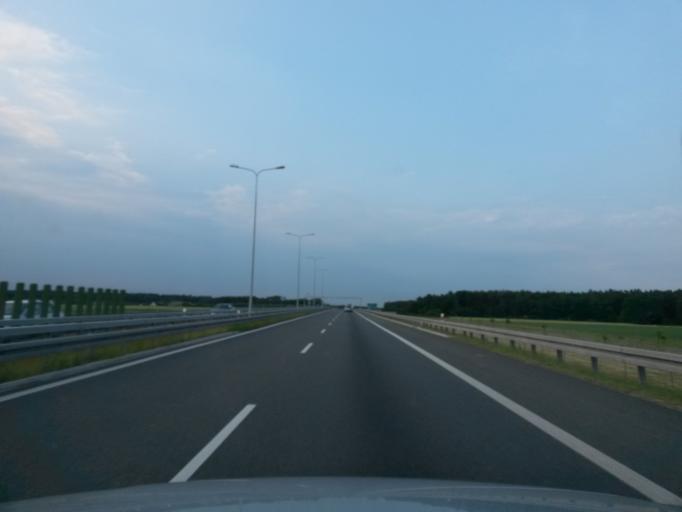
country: PL
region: Lower Silesian Voivodeship
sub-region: Powiat olesnicki
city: Twardogora
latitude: 51.2882
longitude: 17.5769
